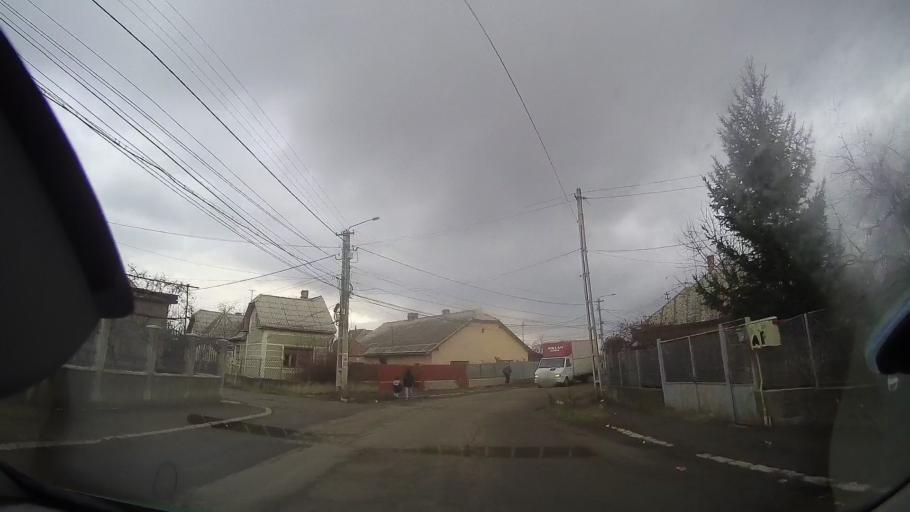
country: RO
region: Cluj
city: Turda
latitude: 46.5573
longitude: 23.7894
